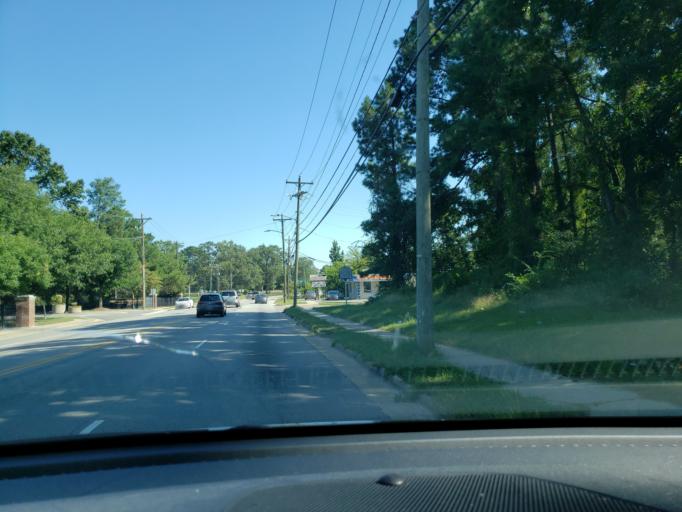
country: US
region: North Carolina
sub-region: Cumberland County
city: Fayetteville
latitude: 35.0688
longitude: -78.8922
